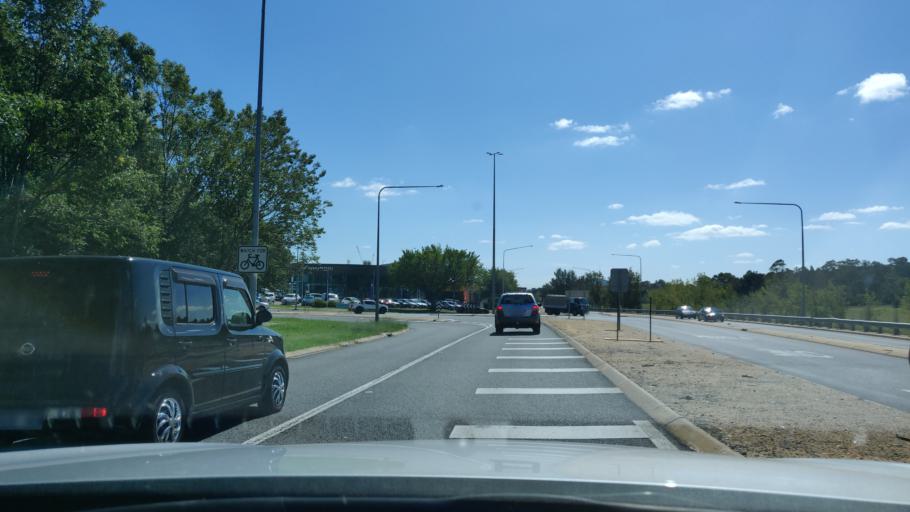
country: AU
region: Australian Capital Territory
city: Forrest
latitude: -35.3580
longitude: 149.0916
